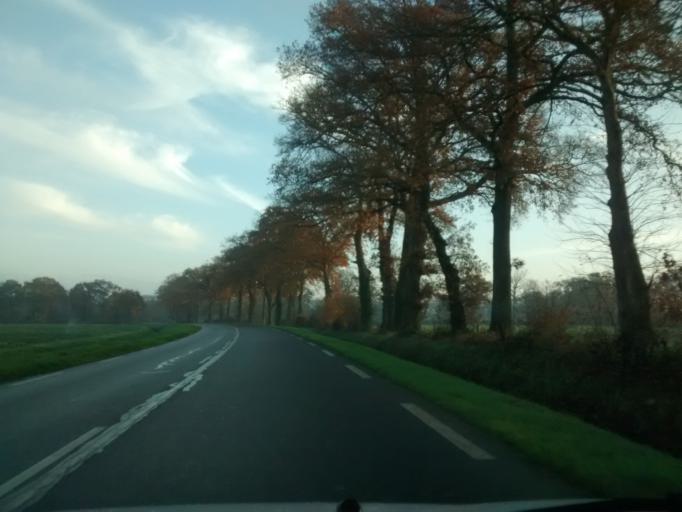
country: FR
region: Brittany
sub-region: Departement d'Ille-et-Vilaine
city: Sens-de-Bretagne
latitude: 48.3058
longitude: -1.5443
